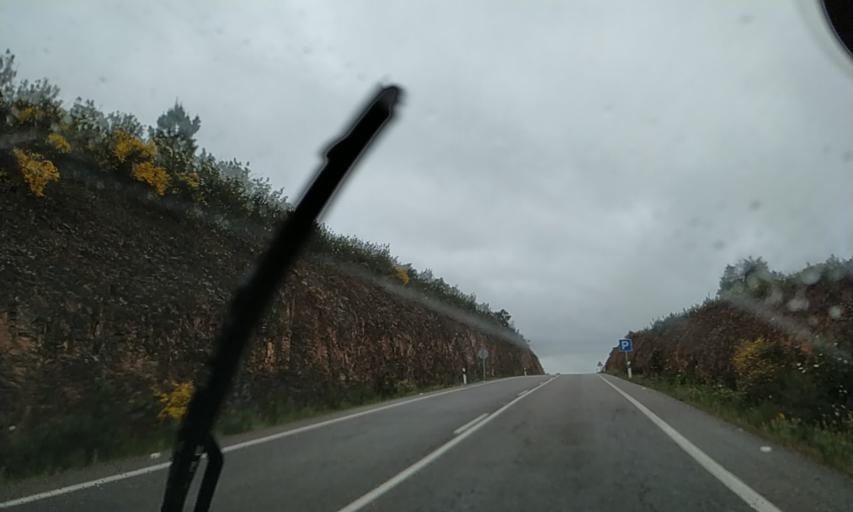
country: ES
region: Extremadura
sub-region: Provincia de Badajoz
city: Puebla de Obando
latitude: 39.1669
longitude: -6.6327
